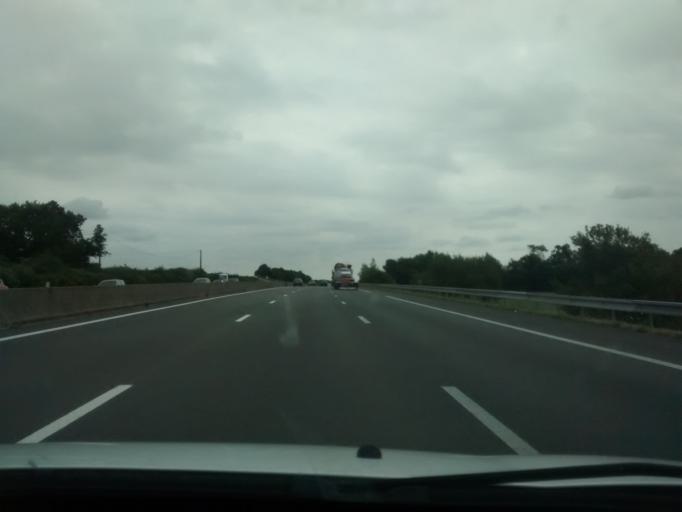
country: FR
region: Centre
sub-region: Departement d'Eure-et-Loir
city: La Bazoche-Gouet
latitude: 48.2265
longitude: 0.9818
